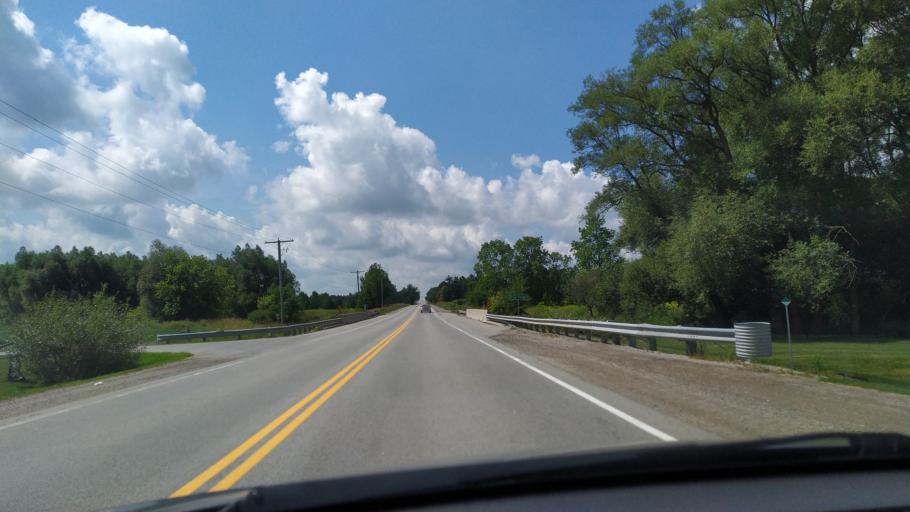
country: CA
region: Ontario
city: South Huron
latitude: 43.3185
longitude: -81.3182
